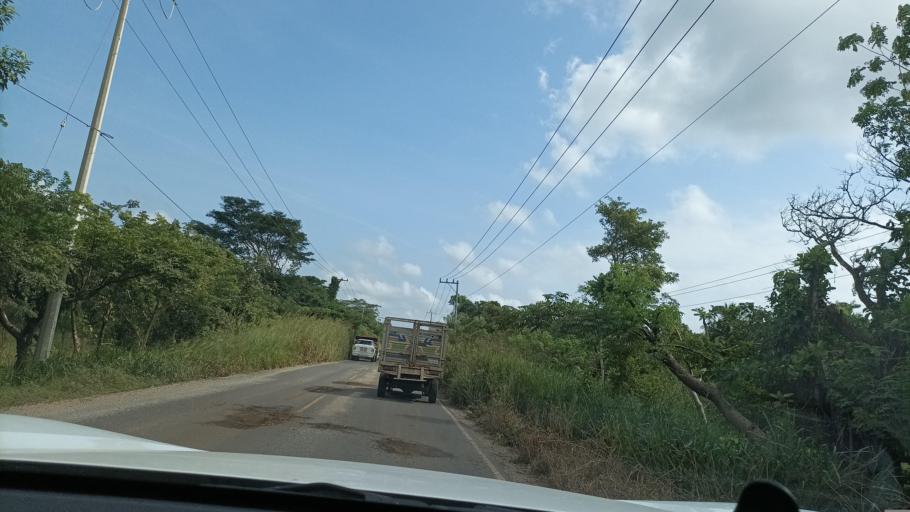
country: MX
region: Veracruz
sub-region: Chinameca
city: Chacalapa
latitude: 18.0704
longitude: -94.6854
